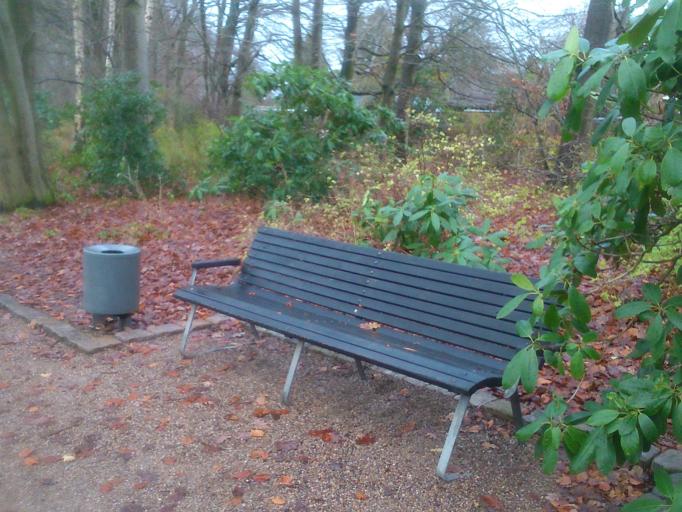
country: DK
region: Central Jutland
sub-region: Ikast-Brande Kommune
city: Ikast
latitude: 56.1414
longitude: 9.1657
